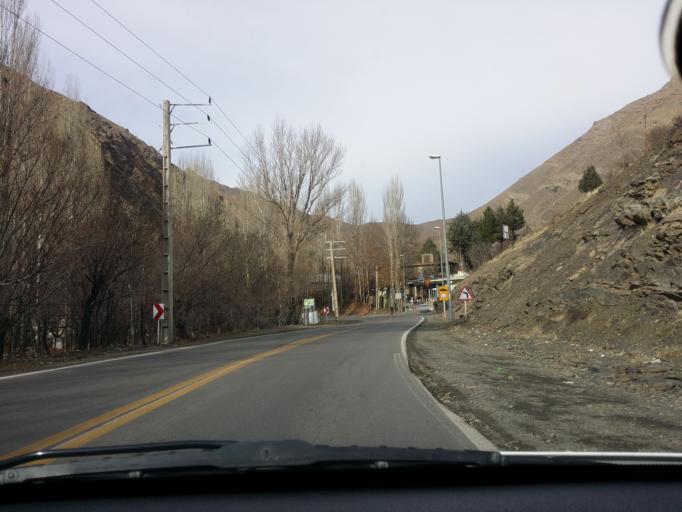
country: IR
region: Alborz
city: Karaj
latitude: 36.0348
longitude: 51.1971
